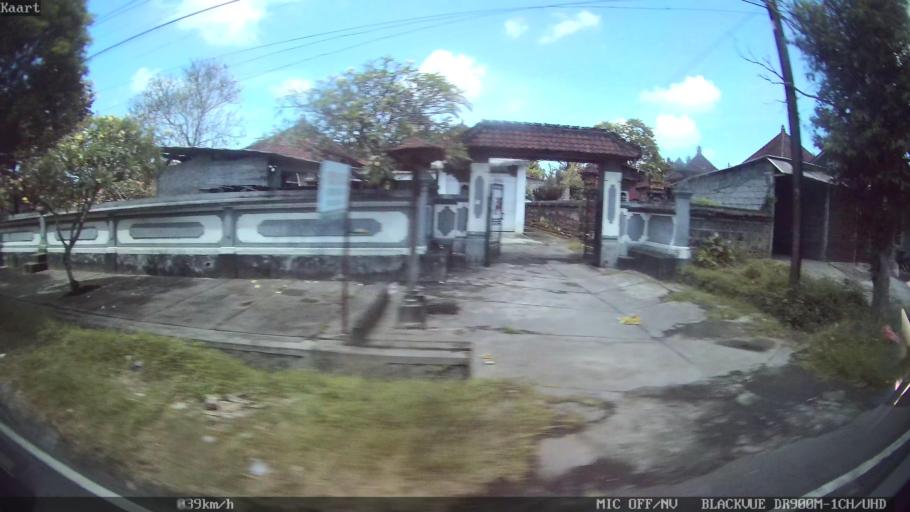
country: ID
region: Bali
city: Banjar Jabejero
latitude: -8.5923
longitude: 115.2622
